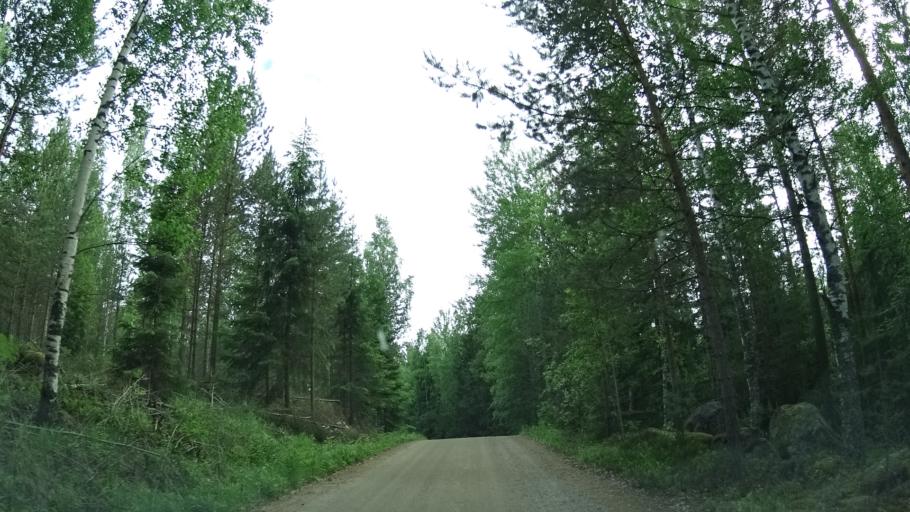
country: FI
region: Central Finland
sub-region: Joutsa
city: Luhanka
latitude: 61.6845
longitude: 25.6871
